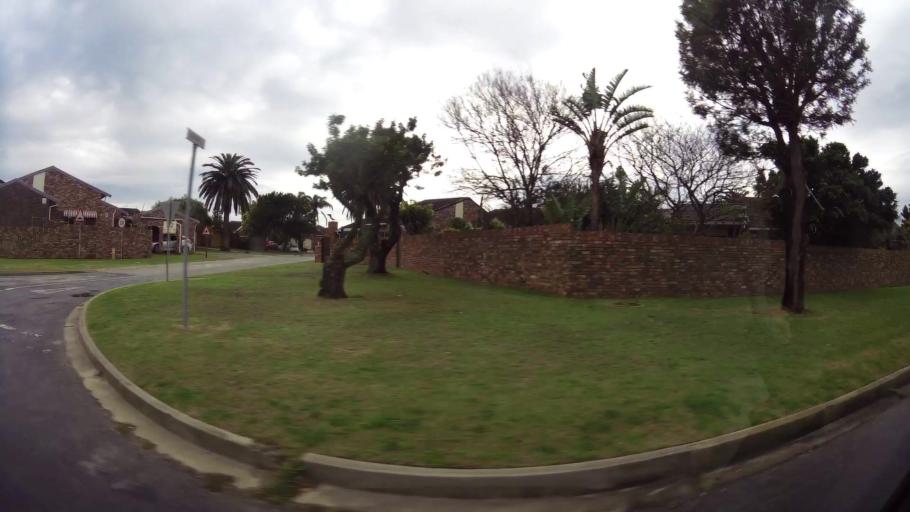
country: ZA
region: Eastern Cape
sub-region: Nelson Mandela Bay Metropolitan Municipality
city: Port Elizabeth
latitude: -33.9737
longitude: 25.6220
